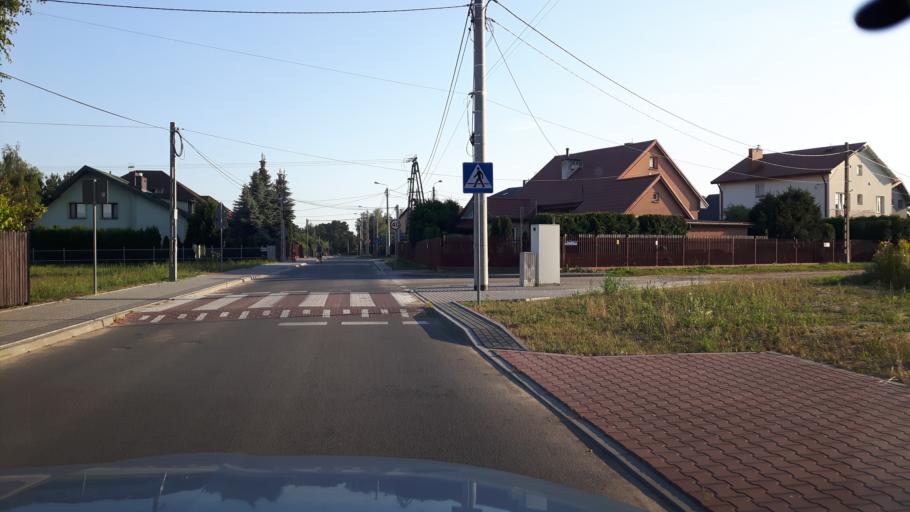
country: PL
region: Masovian Voivodeship
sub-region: Powiat wolominski
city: Kobylka
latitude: 52.3209
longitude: 21.1953
